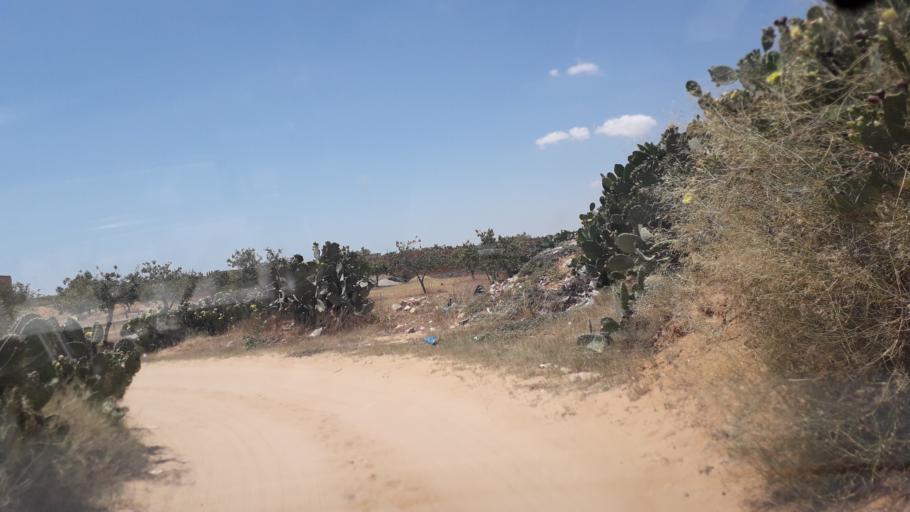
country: TN
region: Safaqis
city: Al Qarmadah
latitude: 34.8307
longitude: 10.7712
